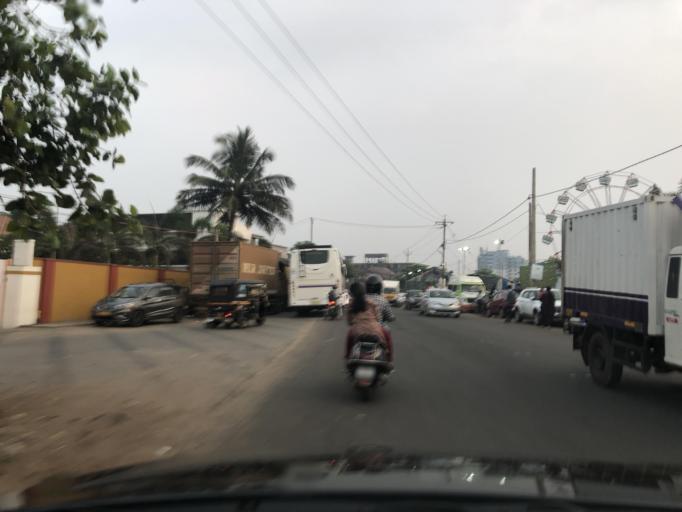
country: IN
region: Kerala
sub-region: Kozhikode
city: Kozhikode
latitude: 11.2508
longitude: 75.7716
